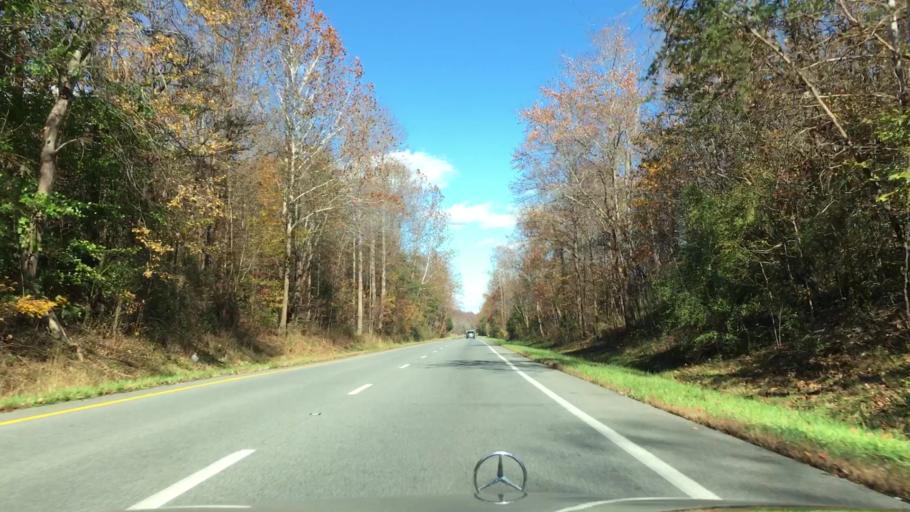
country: US
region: Virginia
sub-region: Albemarle County
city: Crozet
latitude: 37.9090
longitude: -78.6902
